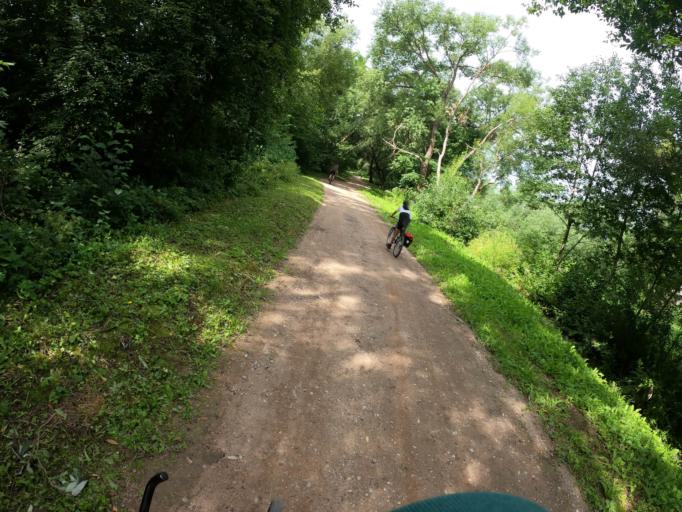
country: LT
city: Kulautuva
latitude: 54.9563
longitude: 23.6254
